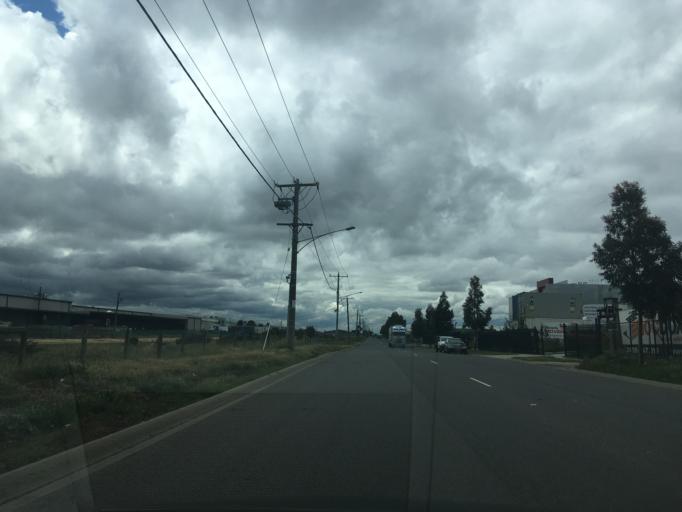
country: AU
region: Victoria
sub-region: Brimbank
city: Sunshine West
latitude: -37.8218
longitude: 144.7973
